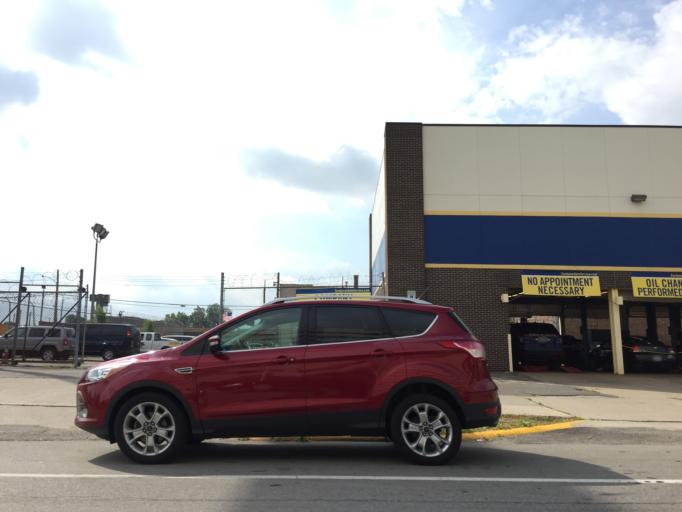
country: US
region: Michigan
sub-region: Wayne County
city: Hamtramck
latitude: 42.3704
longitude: -83.0725
